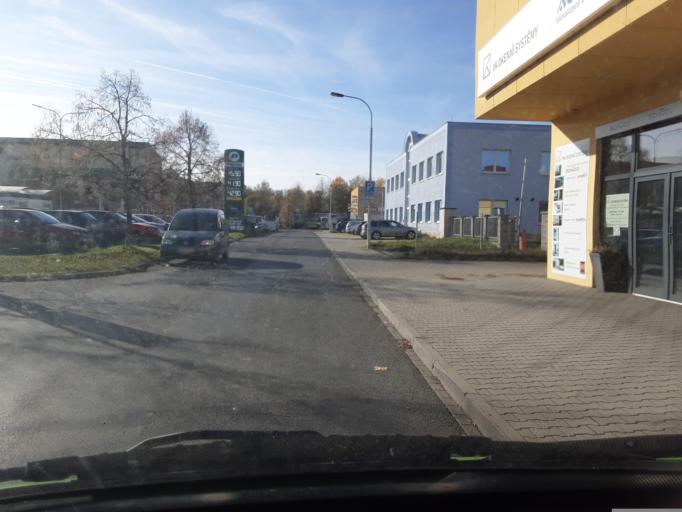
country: CZ
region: Plzensky
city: Klatovy
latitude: 49.3829
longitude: 13.2964
